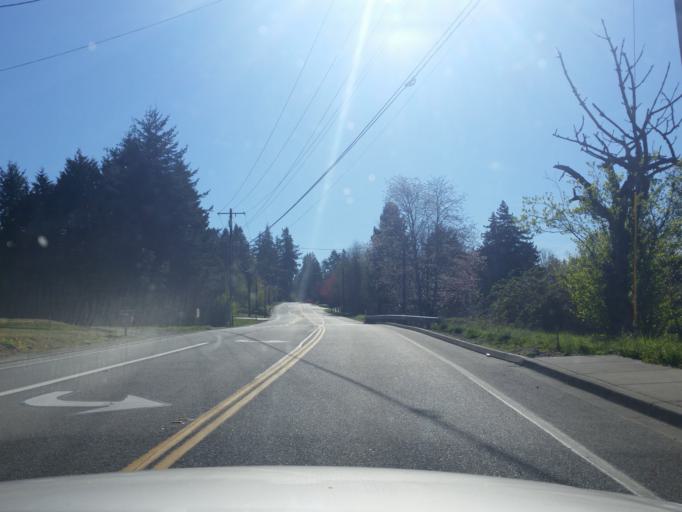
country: US
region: Washington
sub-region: Snohomish County
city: Silver Firs
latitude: 47.8886
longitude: -122.1489
